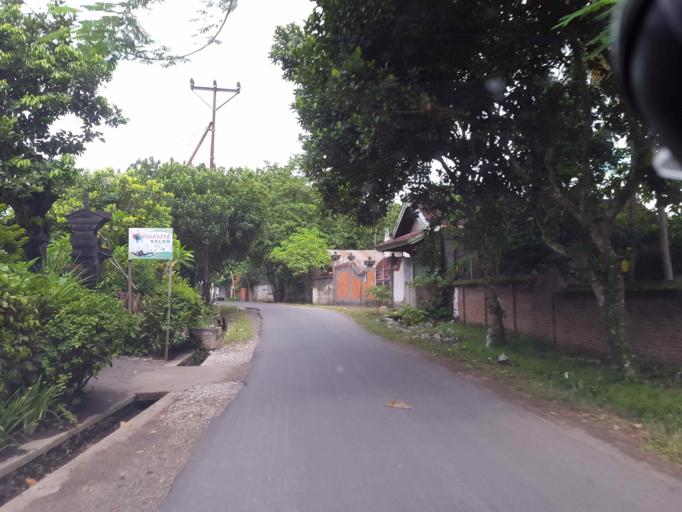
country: ID
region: West Nusa Tenggara
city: Mambalan
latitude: -8.5432
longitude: 116.1095
